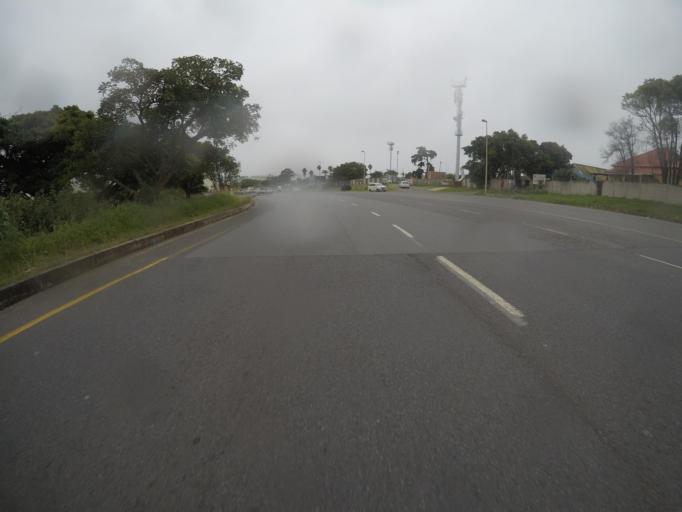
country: ZA
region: Eastern Cape
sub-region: Buffalo City Metropolitan Municipality
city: East London
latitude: -32.9736
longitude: 27.8968
